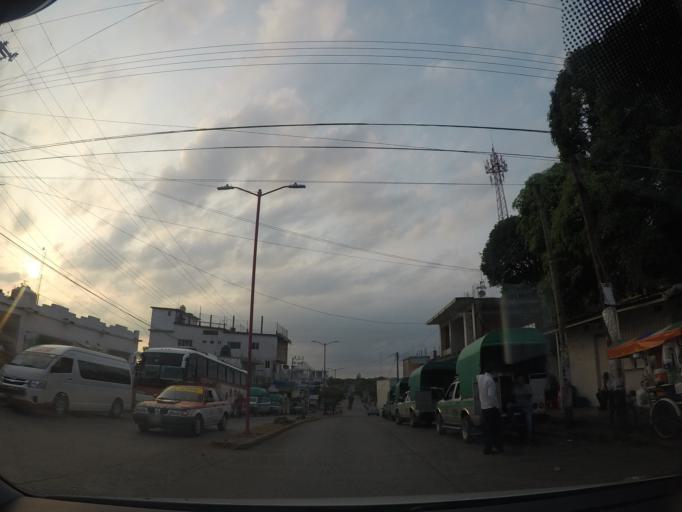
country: MX
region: Oaxaca
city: Matias Romero
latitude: 16.8768
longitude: -95.0409
